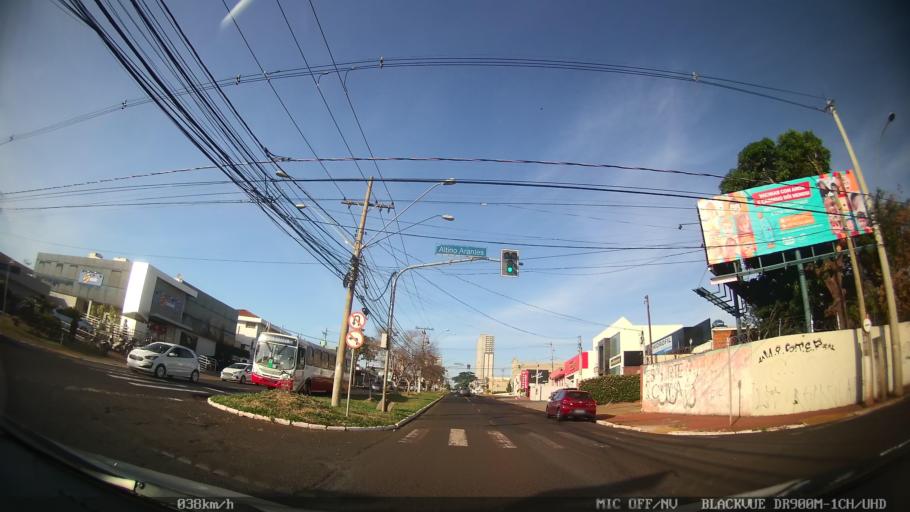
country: BR
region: Sao Paulo
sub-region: Ribeirao Preto
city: Ribeirao Preto
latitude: -21.1914
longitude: -47.8068
